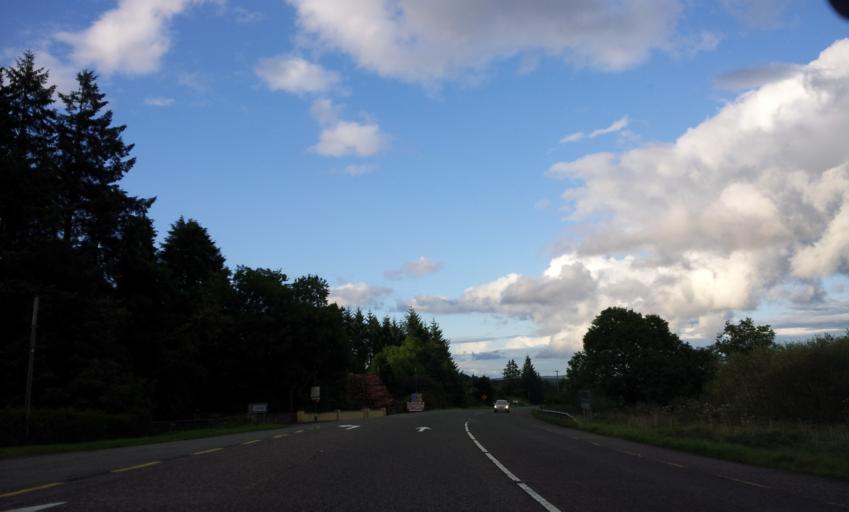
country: IE
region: Munster
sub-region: Ciarrai
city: Castleisland
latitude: 52.2863
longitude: -9.4059
